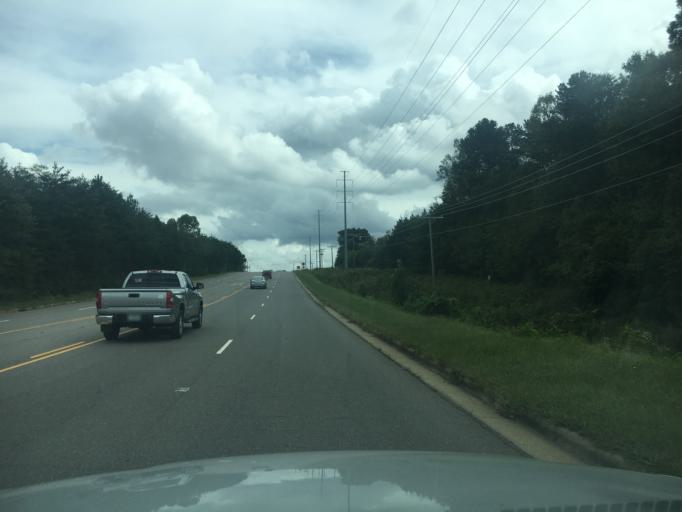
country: US
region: North Carolina
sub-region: Catawba County
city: Hickory
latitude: 35.6991
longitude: -81.2992
